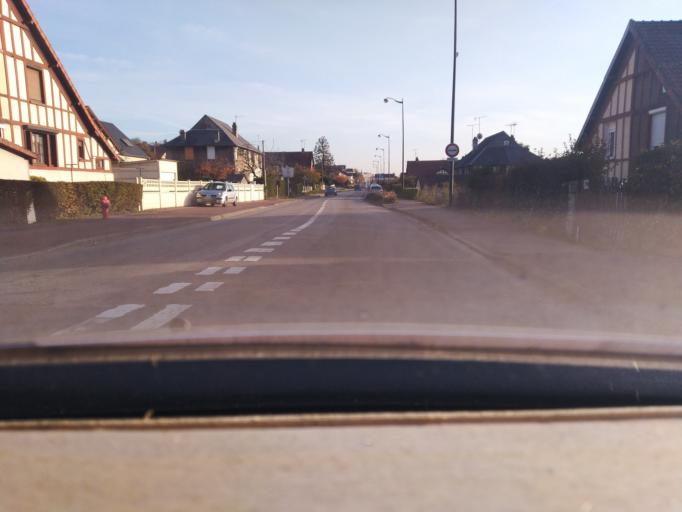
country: FR
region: Haute-Normandie
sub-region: Departement de la Seine-Maritime
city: Le Trait
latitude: 49.4835
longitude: 0.8074
